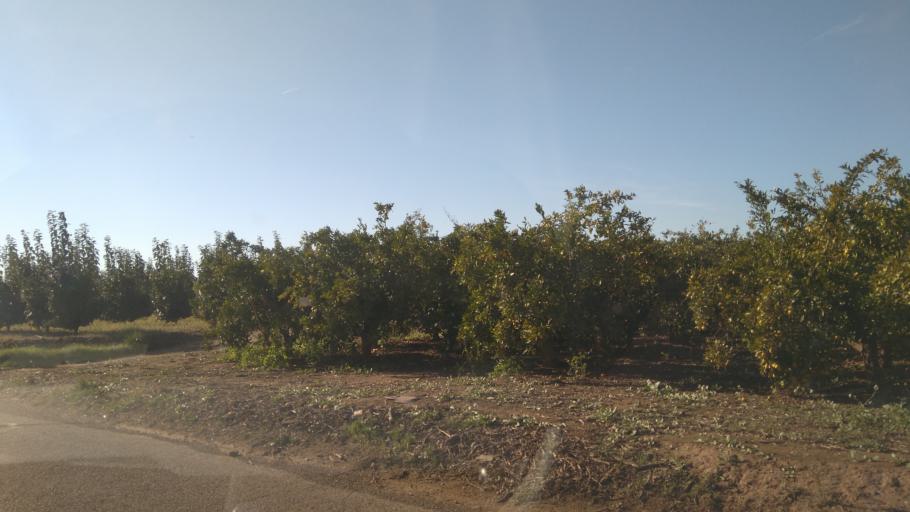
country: ES
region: Valencia
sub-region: Provincia de Valencia
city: L'Alcudia
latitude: 39.1861
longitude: -0.5238
